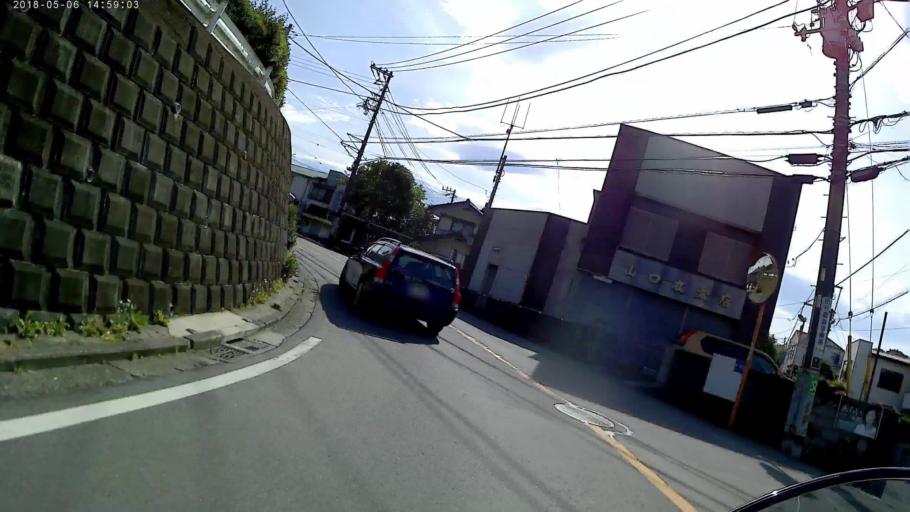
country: JP
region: Kanagawa
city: Yokohama
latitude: 35.4187
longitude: 139.6152
